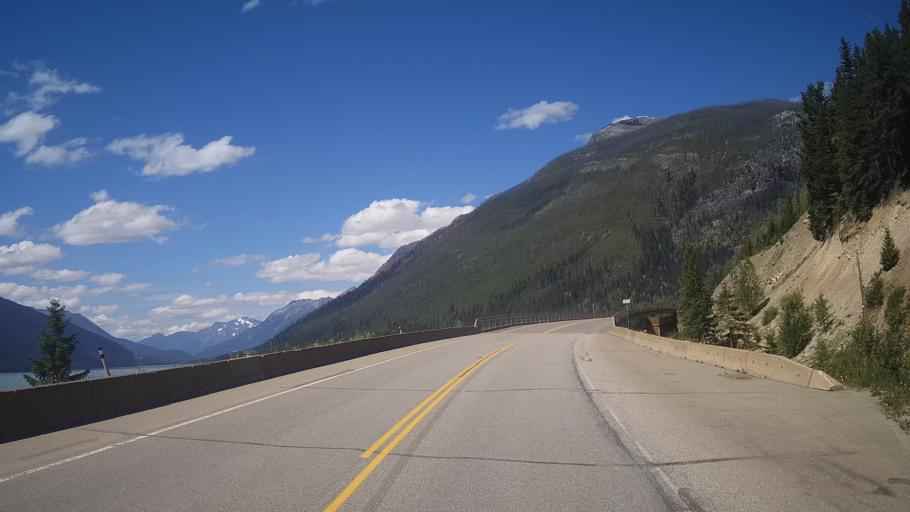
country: CA
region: Alberta
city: Jasper Park Lodge
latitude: 52.9443
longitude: -118.8589
